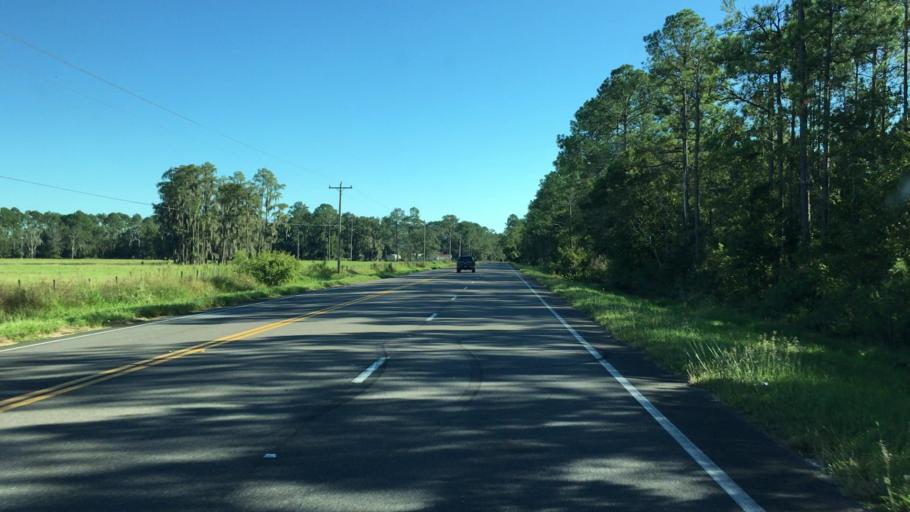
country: US
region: Florida
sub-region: Alachua County
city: Gainesville
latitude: 29.7457
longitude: -82.2772
